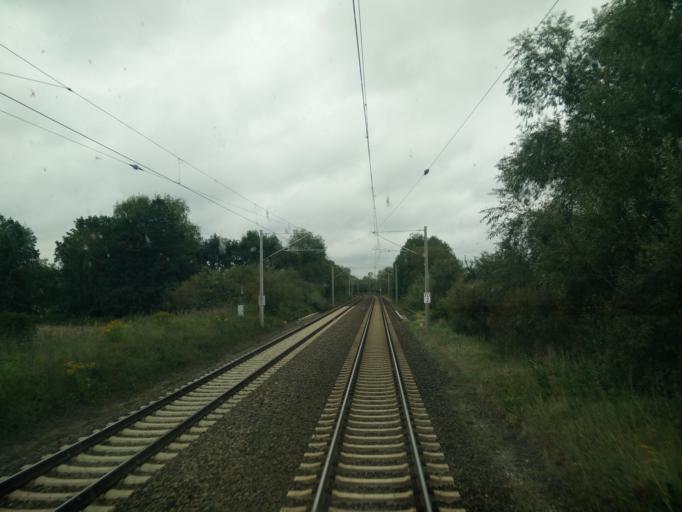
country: DE
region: Brandenburg
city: Luebben
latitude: 51.9611
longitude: 13.8233
